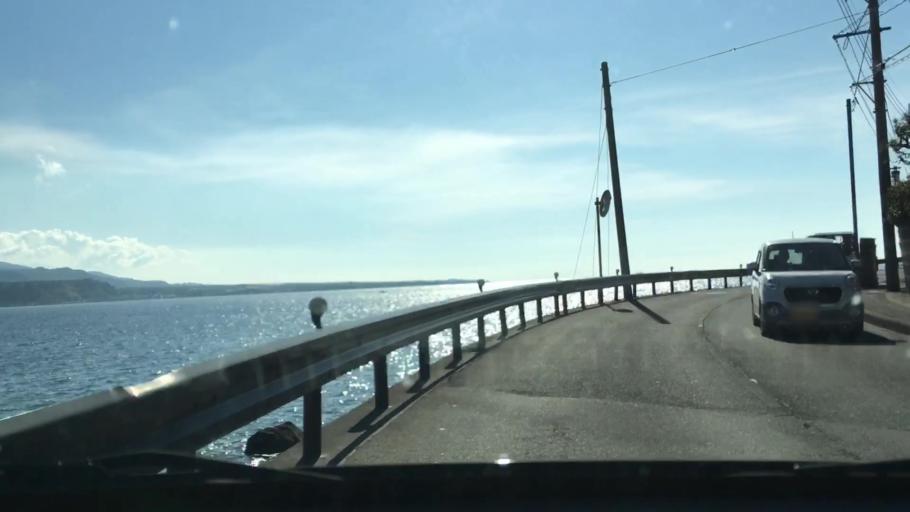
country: JP
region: Kagoshima
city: Kagoshima-shi
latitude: 31.6128
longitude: 130.5749
